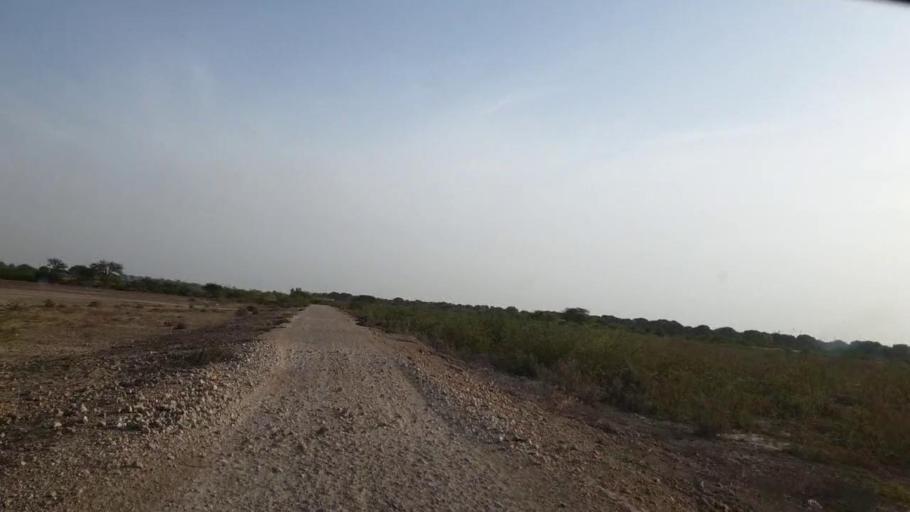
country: PK
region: Sindh
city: Kunri
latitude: 25.0753
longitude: 69.4438
